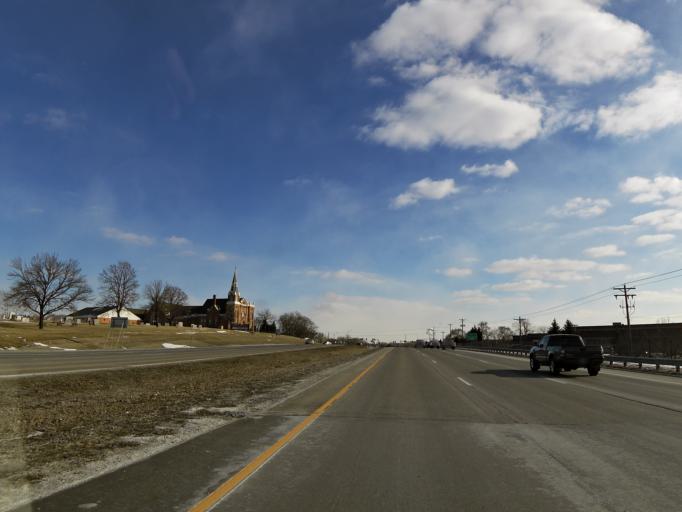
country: US
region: Minnesota
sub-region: Dakota County
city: Mendota Heights
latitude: 44.8508
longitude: -93.1286
